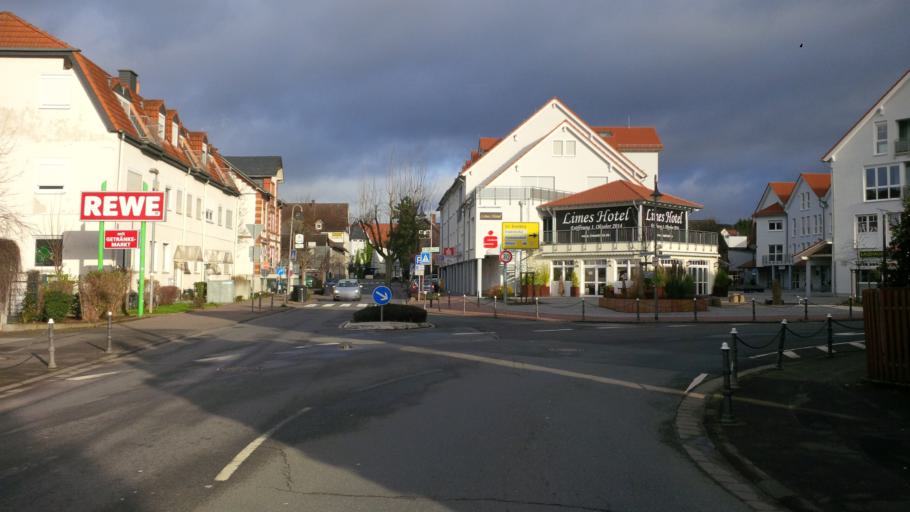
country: DE
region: Hesse
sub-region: Regierungsbezirk Darmstadt
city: Wehrheim
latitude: 50.3026
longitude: 8.5684
